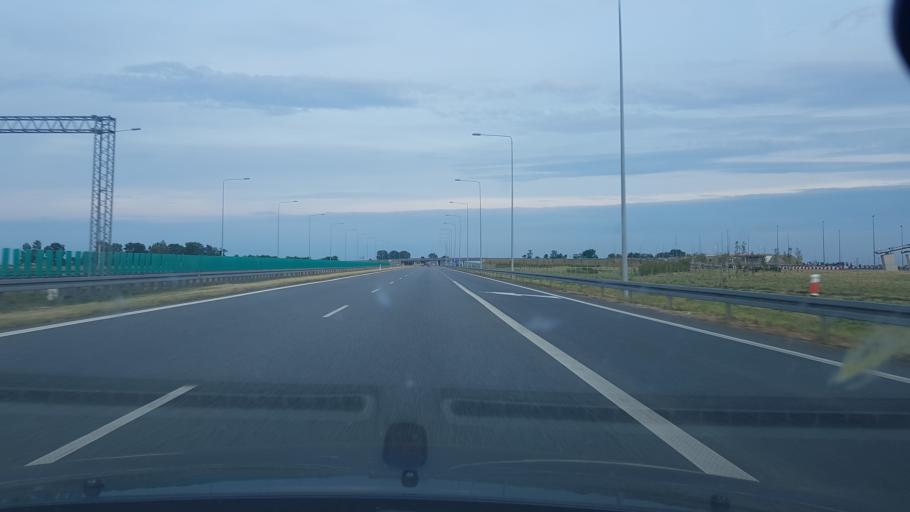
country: PL
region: Lodz Voivodeship
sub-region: Powiat kutnowski
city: Krzyzanow
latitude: 52.2242
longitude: 19.4660
